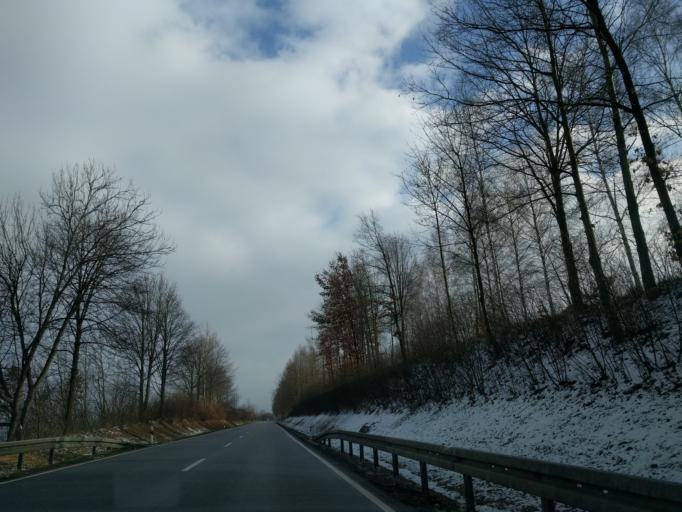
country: DE
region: Bavaria
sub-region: Lower Bavaria
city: Zwiesel
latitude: 49.0039
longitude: 13.2227
